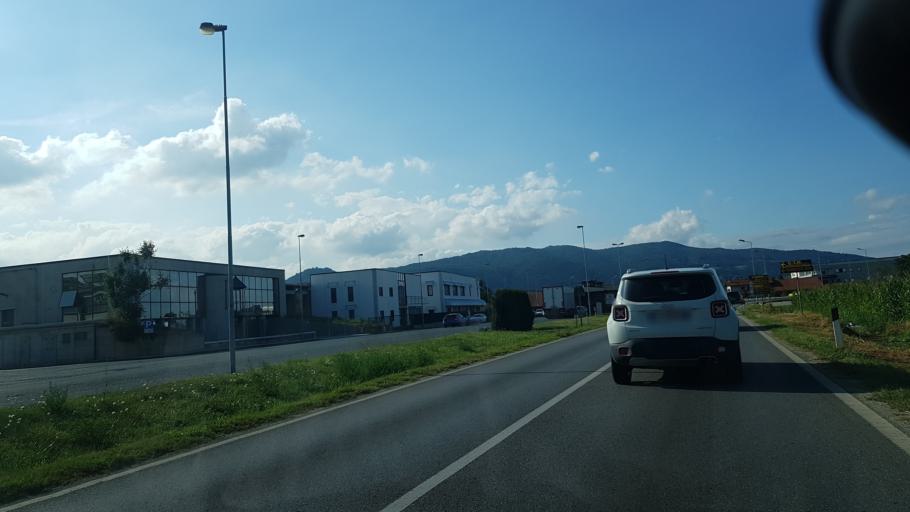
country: IT
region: Piedmont
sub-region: Provincia di Cuneo
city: Busca
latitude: 44.4977
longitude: 7.4934
